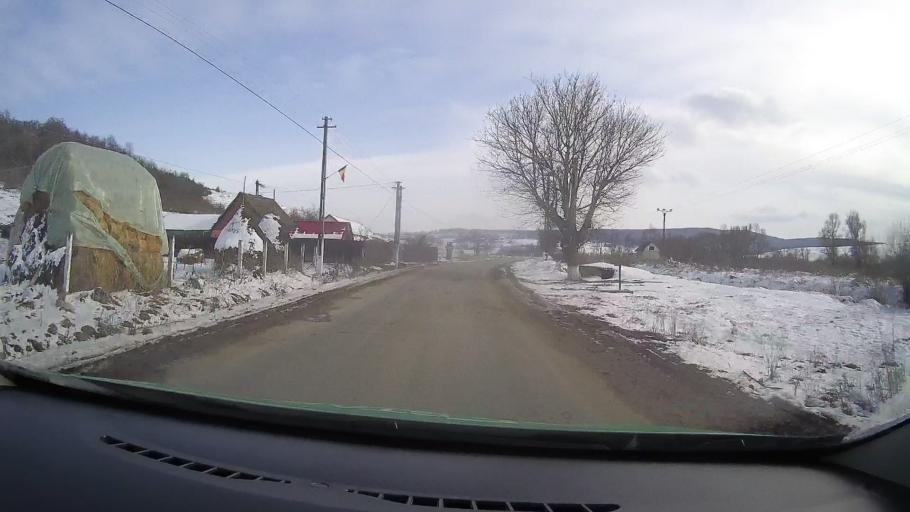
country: RO
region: Sibiu
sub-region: Comuna Iacobeni
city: Iacobeni
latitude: 46.0451
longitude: 24.7261
